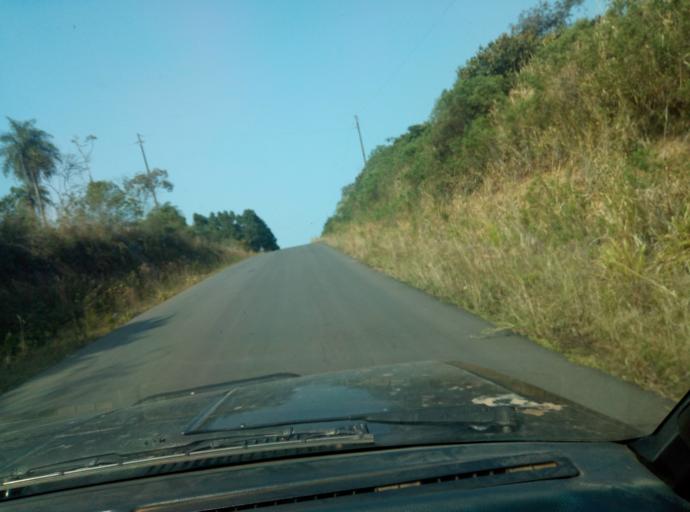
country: PY
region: Caaguazu
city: Carayao
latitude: -25.2438
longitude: -56.2880
